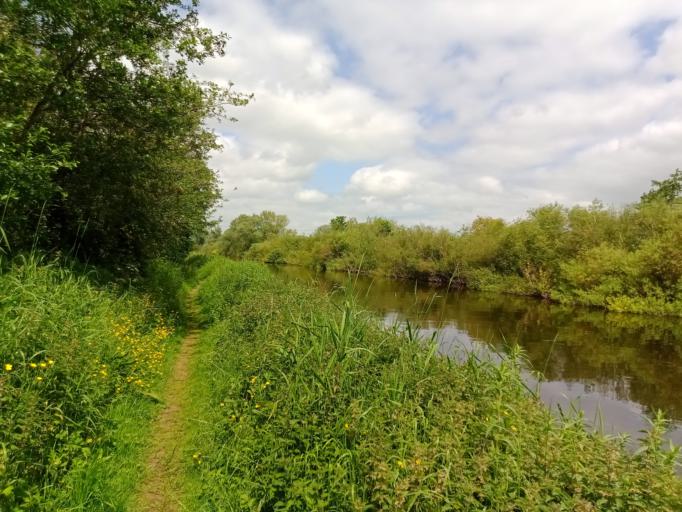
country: IE
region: Leinster
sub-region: County Carlow
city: Carlow
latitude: 52.7954
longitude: -6.9611
